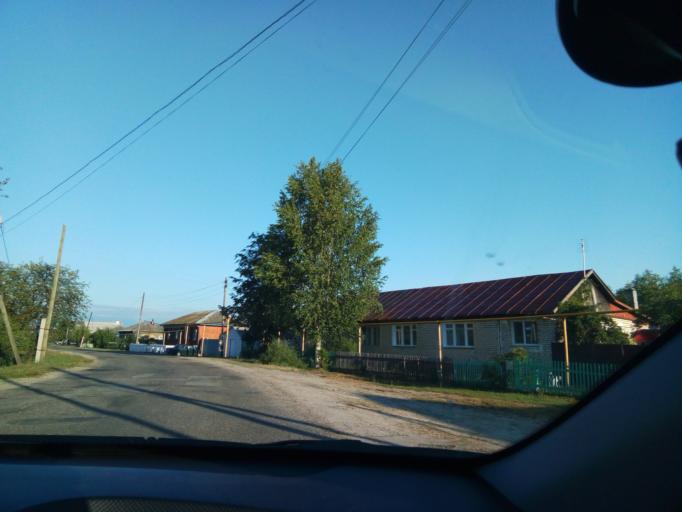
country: RU
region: Nizjnij Novgorod
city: Voznesenskoye
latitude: 54.8881
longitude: 42.7832
